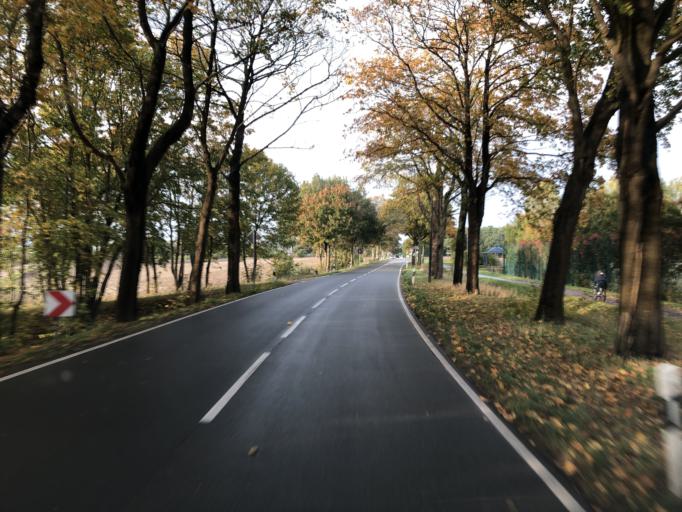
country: DE
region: Lower Saxony
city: Neu Wulmstorf
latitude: 53.4482
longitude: 9.7995
